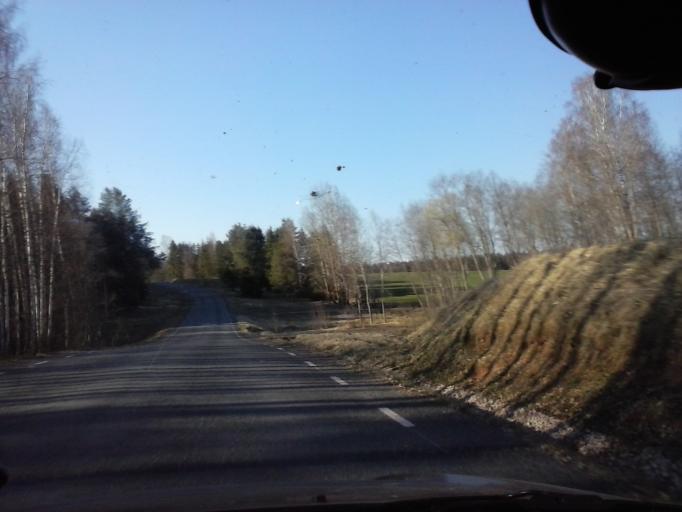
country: EE
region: Tartu
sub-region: UElenurme vald
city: Ulenurme
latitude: 58.1743
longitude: 26.8330
